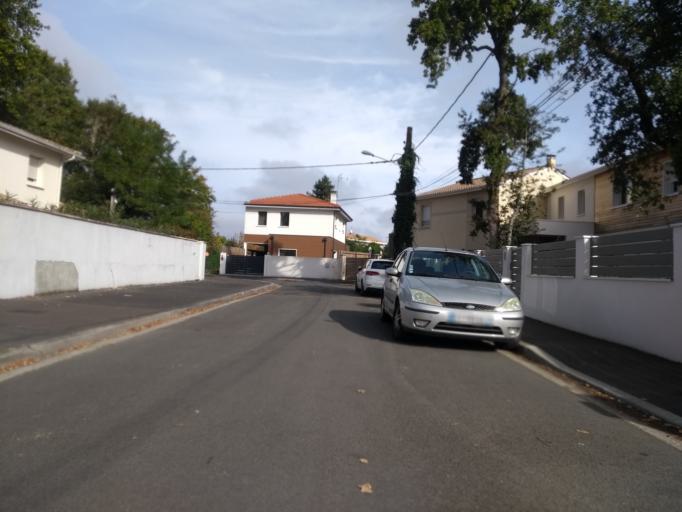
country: FR
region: Aquitaine
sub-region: Departement de la Gironde
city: Pessac
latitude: 44.7939
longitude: -0.6396
